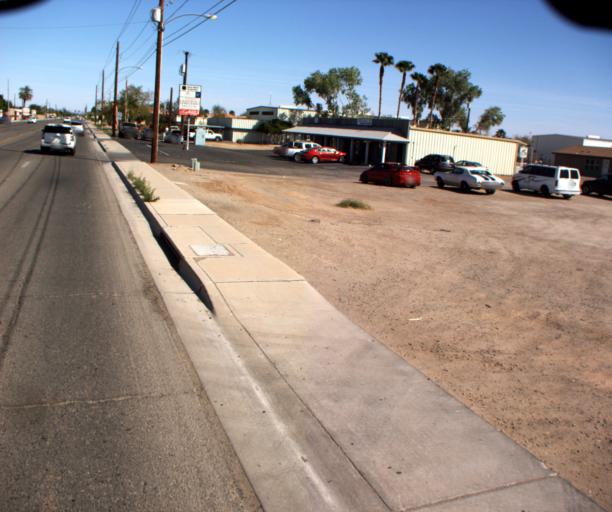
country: US
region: Arizona
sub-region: Yuma County
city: Yuma
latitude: 32.6723
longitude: -114.6501
